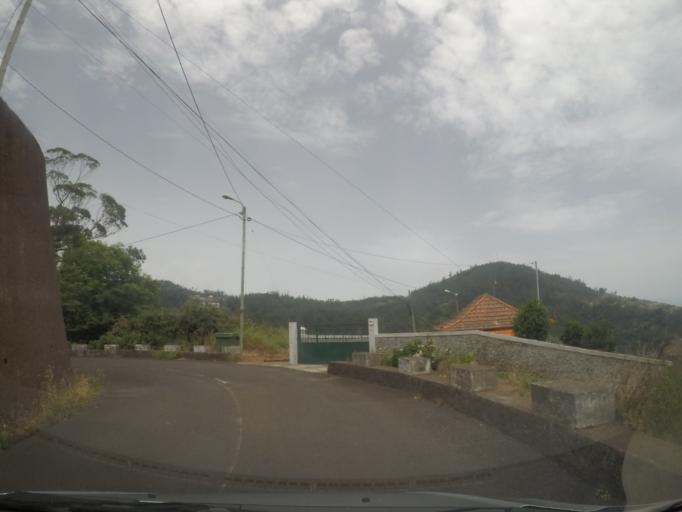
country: PT
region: Madeira
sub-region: Santa Cruz
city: Camacha
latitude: 32.6808
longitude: -16.8423
